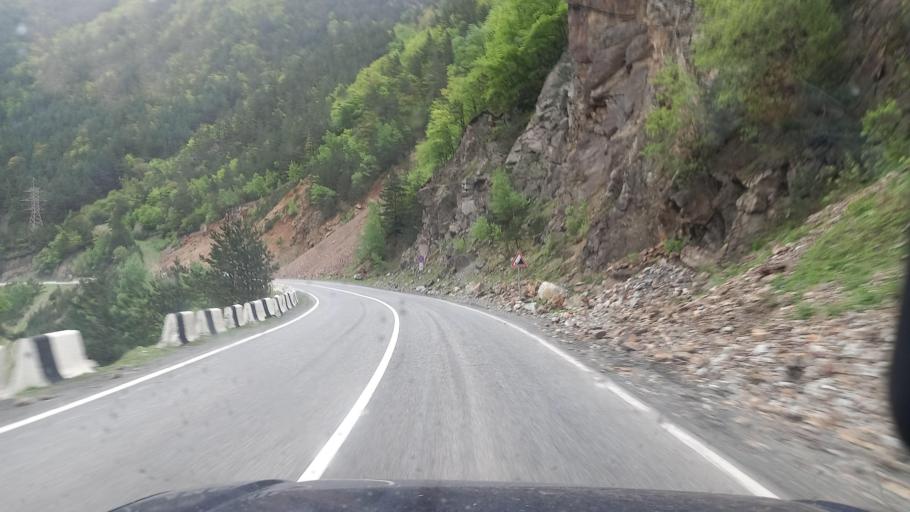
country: RU
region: North Ossetia
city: Mizur
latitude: 42.8094
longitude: 44.0210
